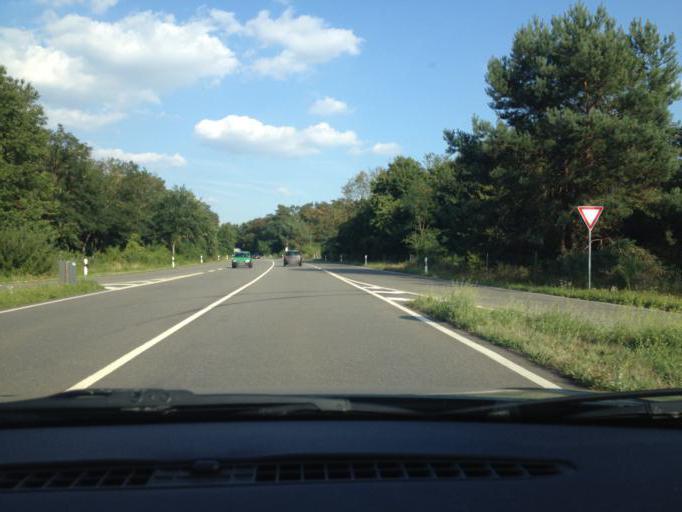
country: DE
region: Rheinland-Pfalz
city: Hanhofen
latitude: 49.3183
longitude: 8.3584
